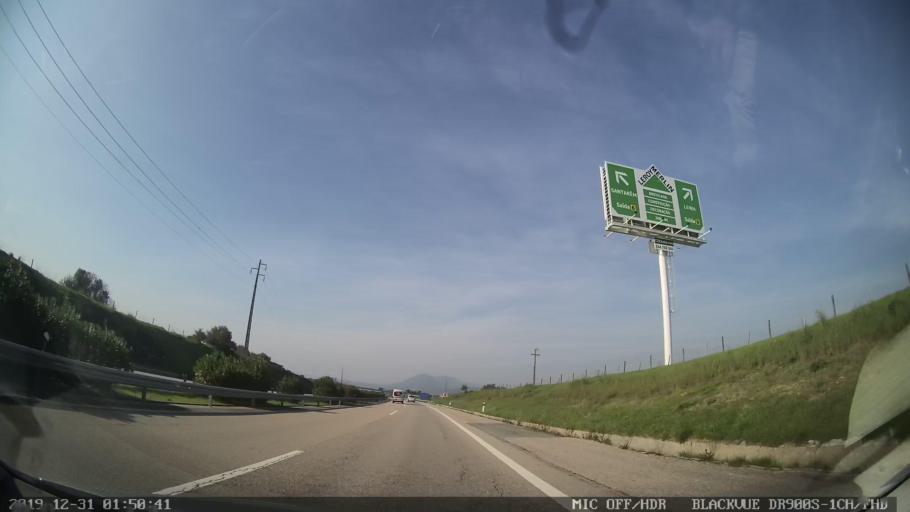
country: PT
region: Santarem
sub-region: Alcanena
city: Alcanena
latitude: 39.4785
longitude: -8.6115
